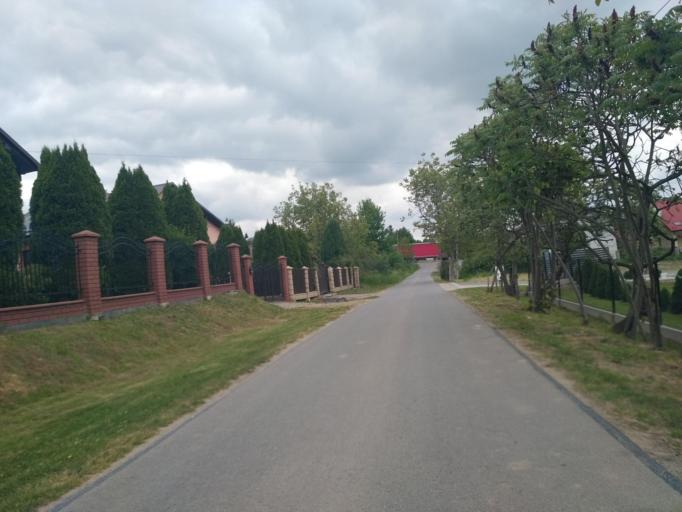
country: PL
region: Subcarpathian Voivodeship
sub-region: Powiat krosnienski
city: Jedlicze
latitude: 49.7213
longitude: 21.6932
